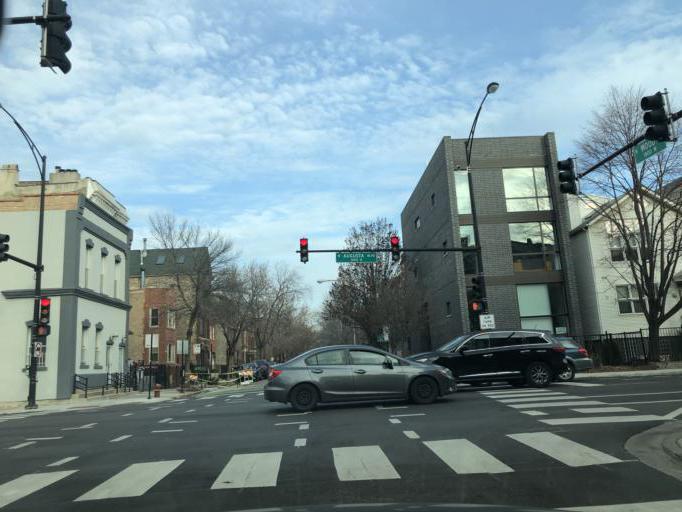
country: US
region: Illinois
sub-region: Cook County
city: Chicago
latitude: 41.8995
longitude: -87.6723
